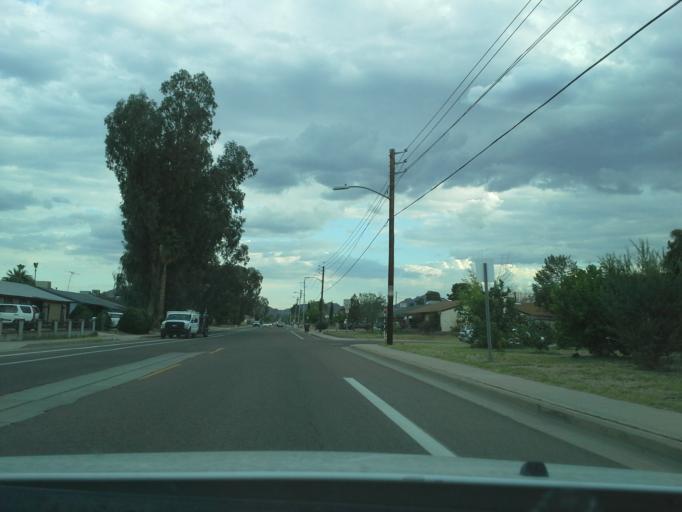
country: US
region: Arizona
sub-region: Maricopa County
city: Paradise Valley
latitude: 33.6106
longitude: -112.0047
